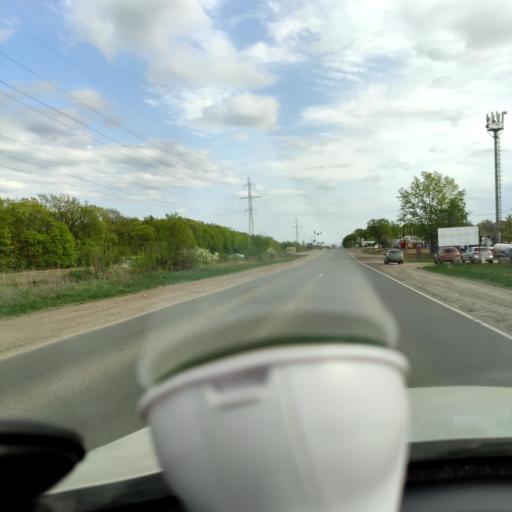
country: RU
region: Samara
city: Novosemeykino
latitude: 53.3341
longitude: 50.2541
